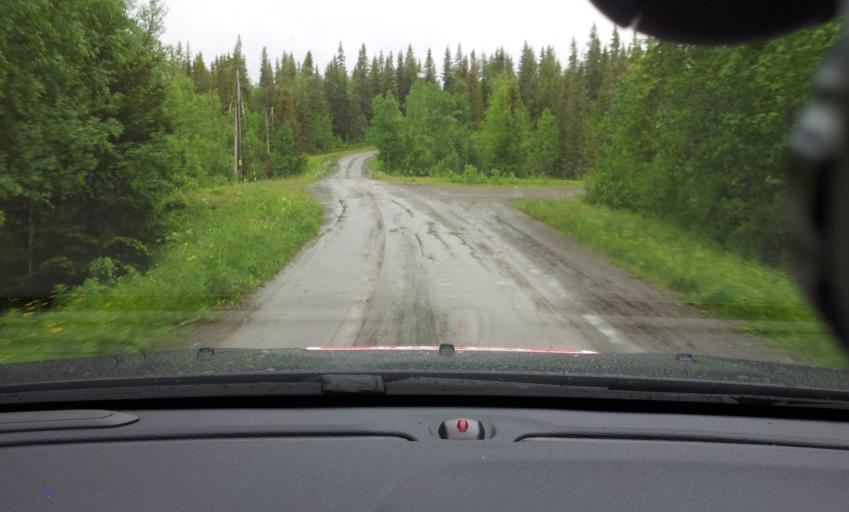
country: SE
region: Jaemtland
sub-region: Are Kommun
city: Are
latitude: 63.5092
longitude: 12.7122
